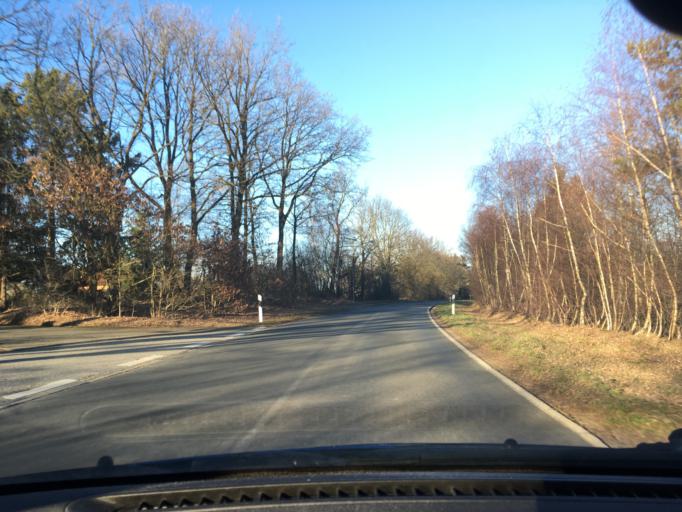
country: DE
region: Schleswig-Holstein
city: Mussen
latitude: 53.4876
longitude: 10.5589
